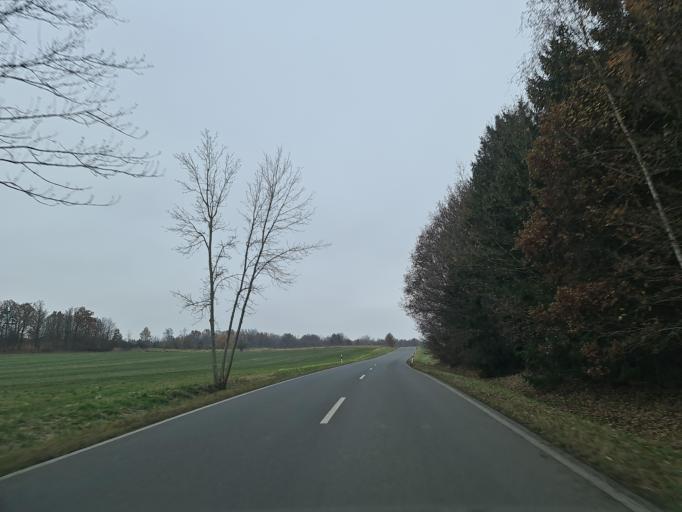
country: DE
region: Saxony
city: Syrau
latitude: 50.5126
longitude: 12.0775
